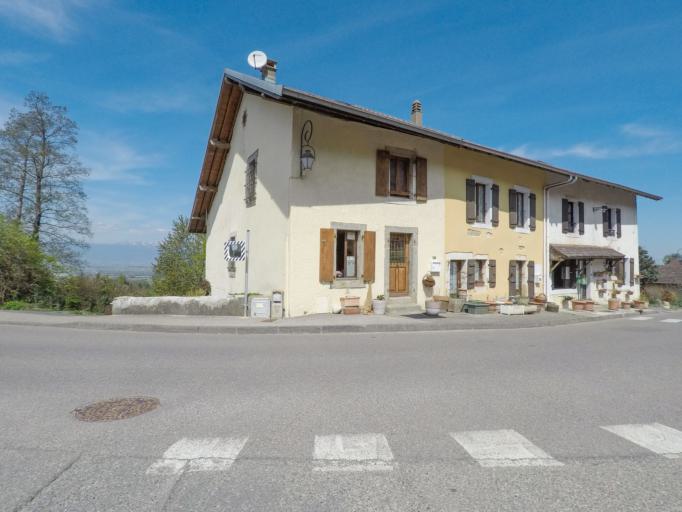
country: FR
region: Rhone-Alpes
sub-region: Departement de la Haute-Savoie
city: Collonges-sous-Saleve
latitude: 46.1284
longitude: 6.1505
